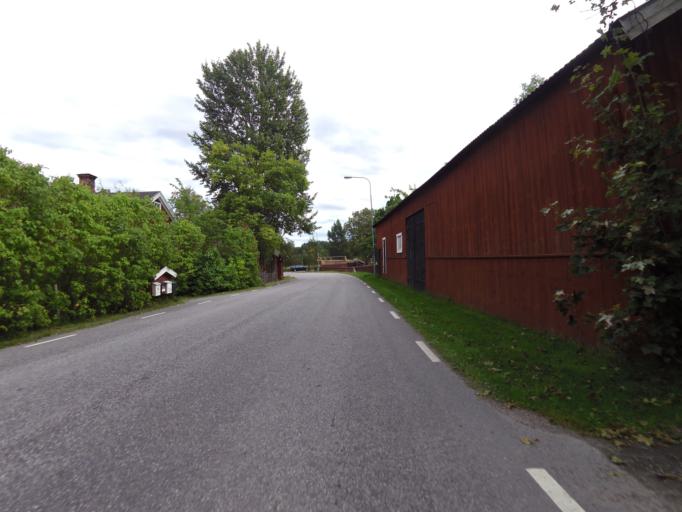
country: SE
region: Gaevleborg
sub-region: Gavle Kommun
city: Valbo
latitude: 60.6492
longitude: 16.9907
